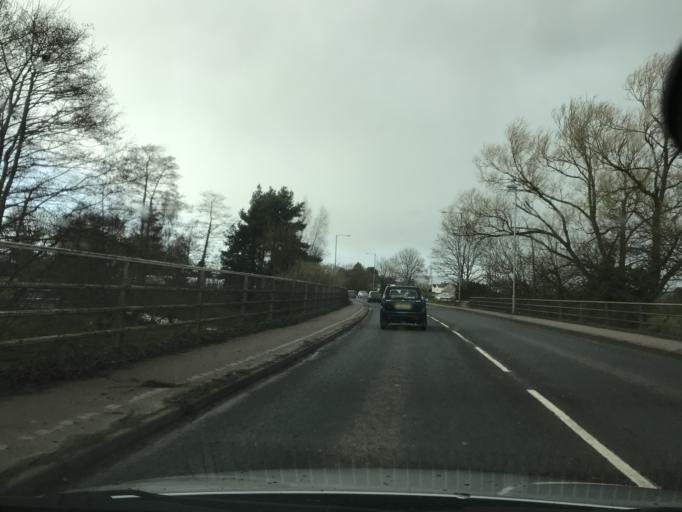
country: GB
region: England
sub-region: Somerset
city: Taunton
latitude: 51.0187
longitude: -3.1301
